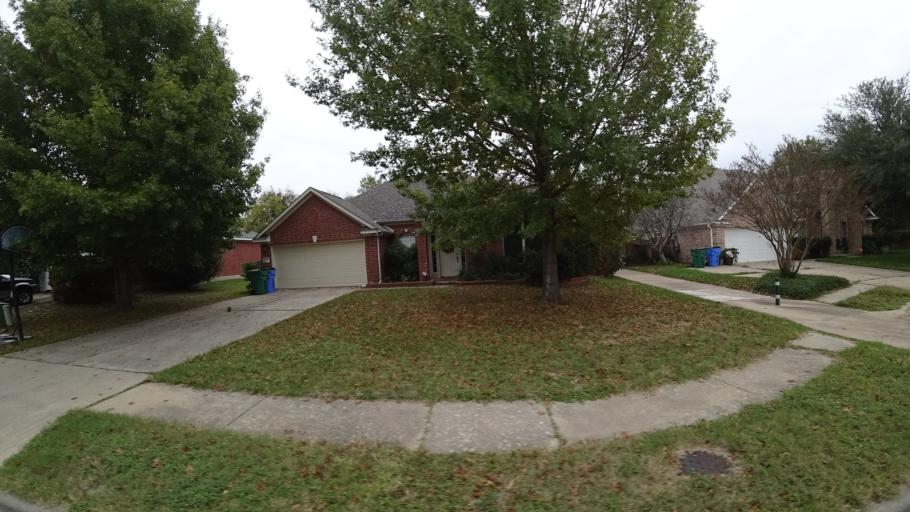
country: US
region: Texas
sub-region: Travis County
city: Pflugerville
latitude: 30.4310
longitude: -97.6232
